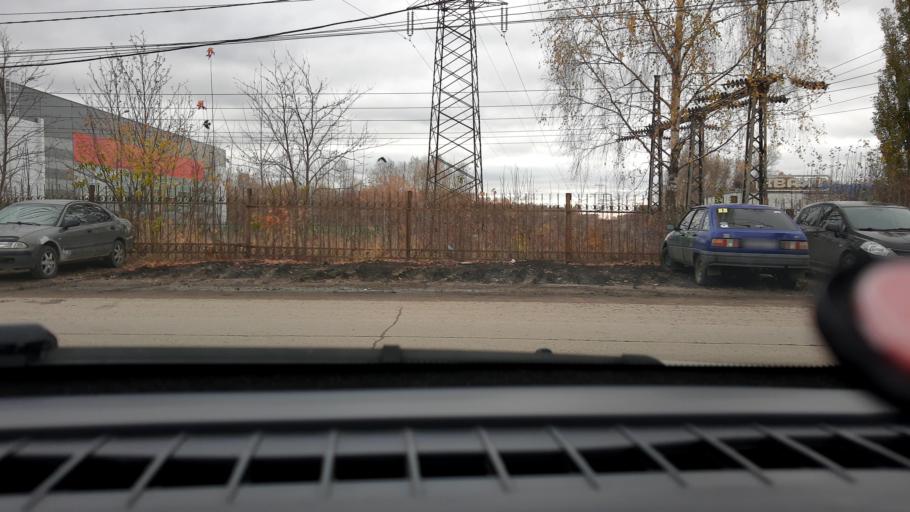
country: RU
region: Nizjnij Novgorod
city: Nizhniy Novgorod
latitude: 56.2297
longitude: 43.9402
